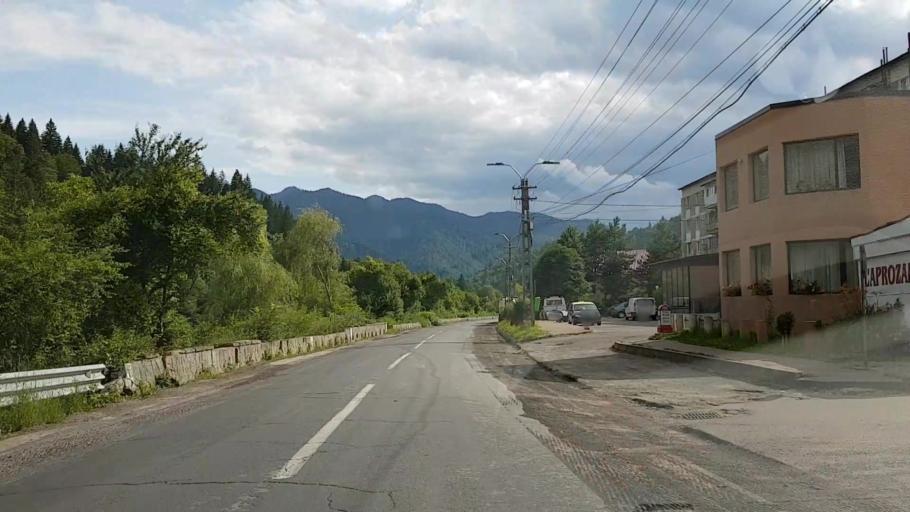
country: RO
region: Neamt
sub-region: Comuna Bicaz
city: Dodeni
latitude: 46.9256
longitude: 26.0936
